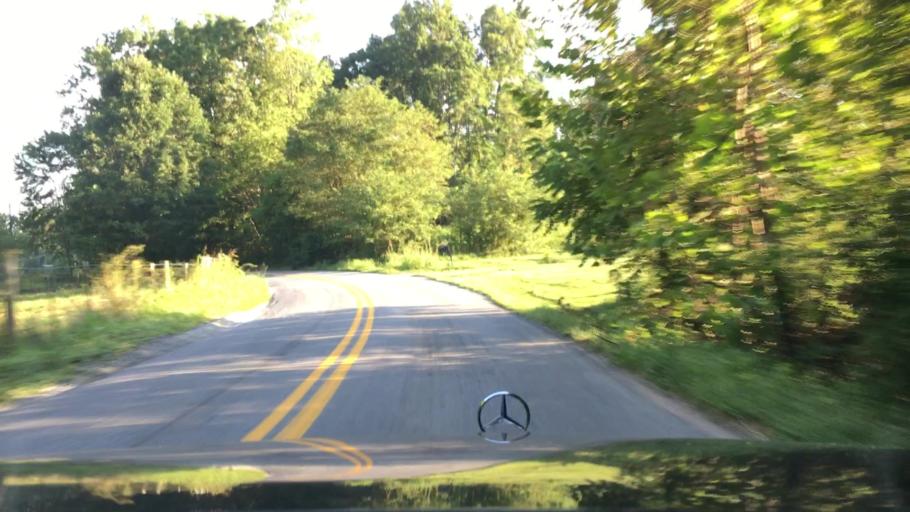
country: US
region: Virginia
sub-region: Campbell County
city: Timberlake
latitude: 37.2778
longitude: -79.2685
